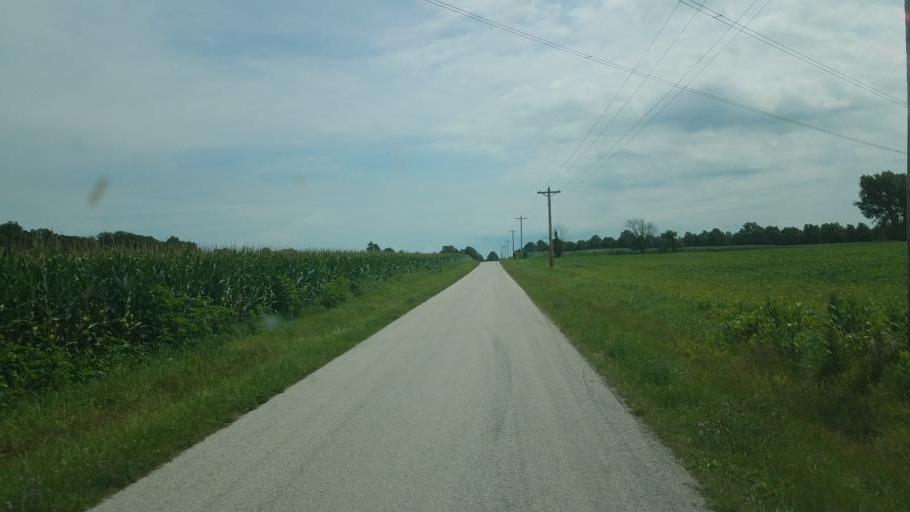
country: US
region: Ohio
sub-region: Crawford County
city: Bucyrus
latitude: 40.8774
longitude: -83.1088
